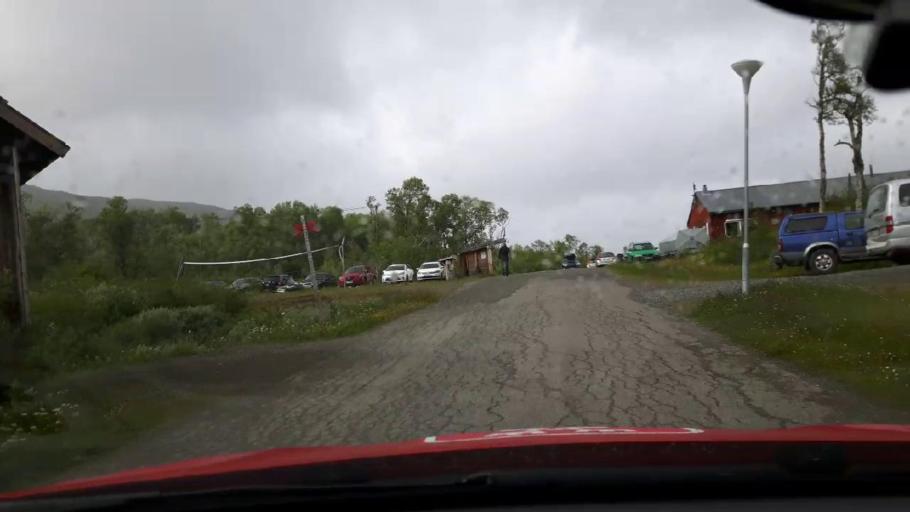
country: NO
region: Nord-Trondelag
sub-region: Meraker
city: Meraker
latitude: 63.1698
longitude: 12.3624
